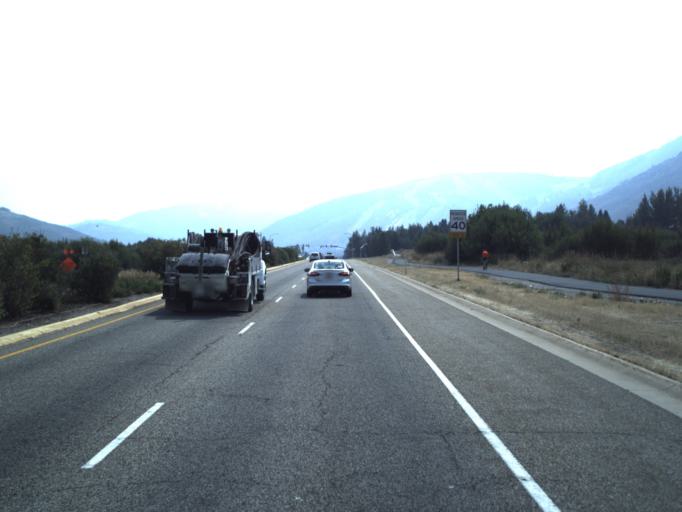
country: US
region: Utah
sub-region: Summit County
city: Park City
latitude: 40.6715
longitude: -111.5173
